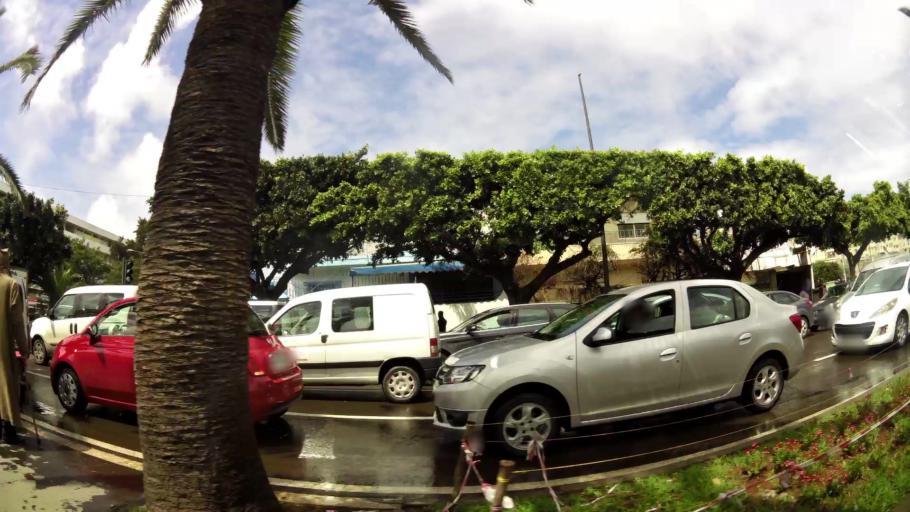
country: MA
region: Grand Casablanca
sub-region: Casablanca
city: Casablanca
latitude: 33.5712
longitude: -7.6357
